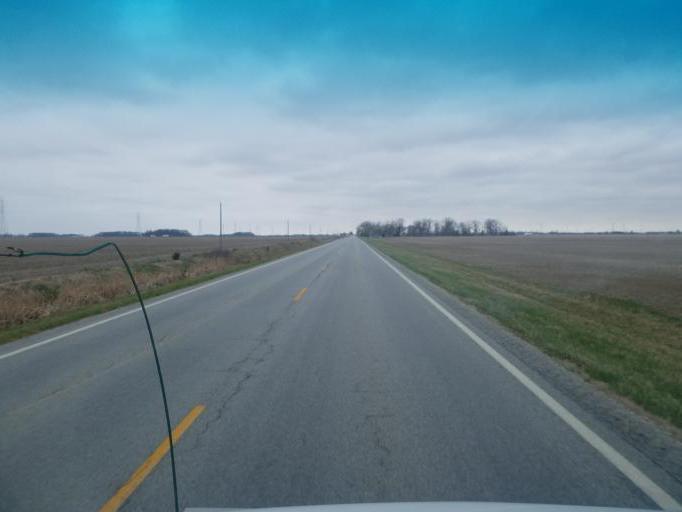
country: US
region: Ohio
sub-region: Van Wert County
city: Van Wert
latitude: 40.9321
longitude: -84.4619
